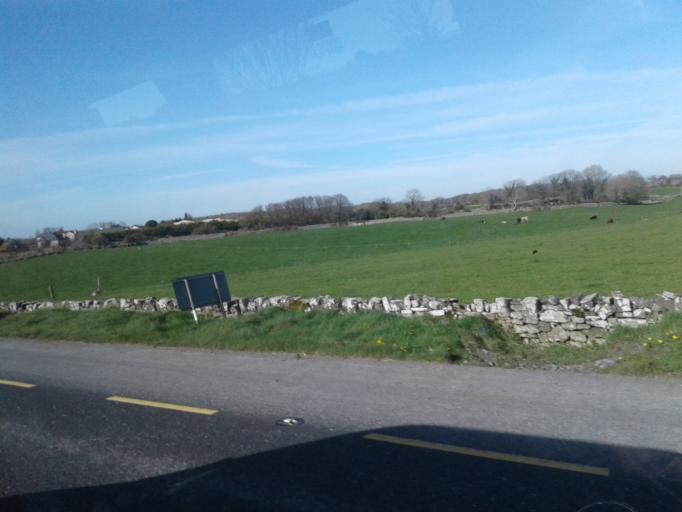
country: IE
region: Connaught
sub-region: County Galway
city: Gort
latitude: 53.1602
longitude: -8.8101
